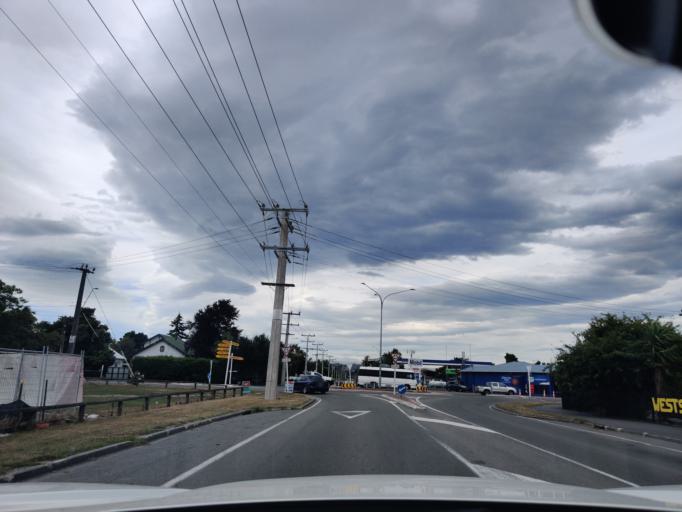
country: NZ
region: Wellington
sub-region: Masterton District
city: Masterton
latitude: -40.9468
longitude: 175.6368
